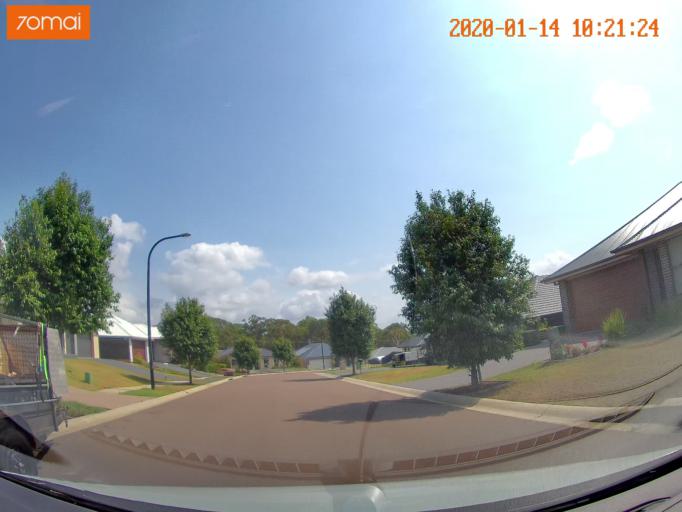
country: AU
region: New South Wales
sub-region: Lake Macquarie Shire
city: Dora Creek
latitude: -33.1098
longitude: 151.5075
